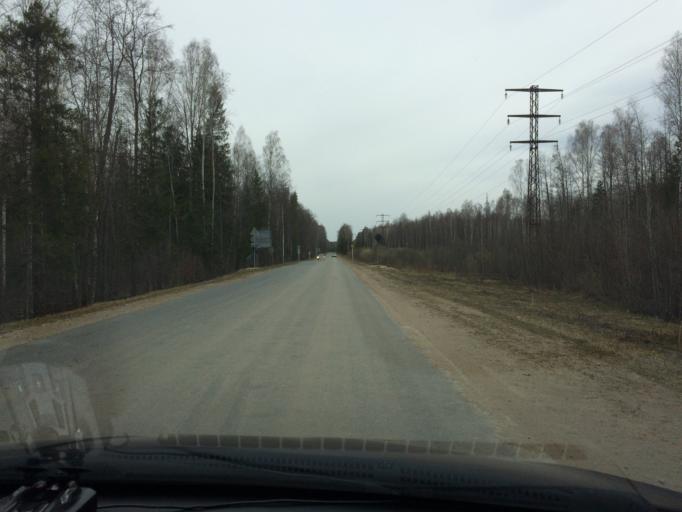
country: RU
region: Mariy-El
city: Surok
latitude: 56.5525
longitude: 48.3148
